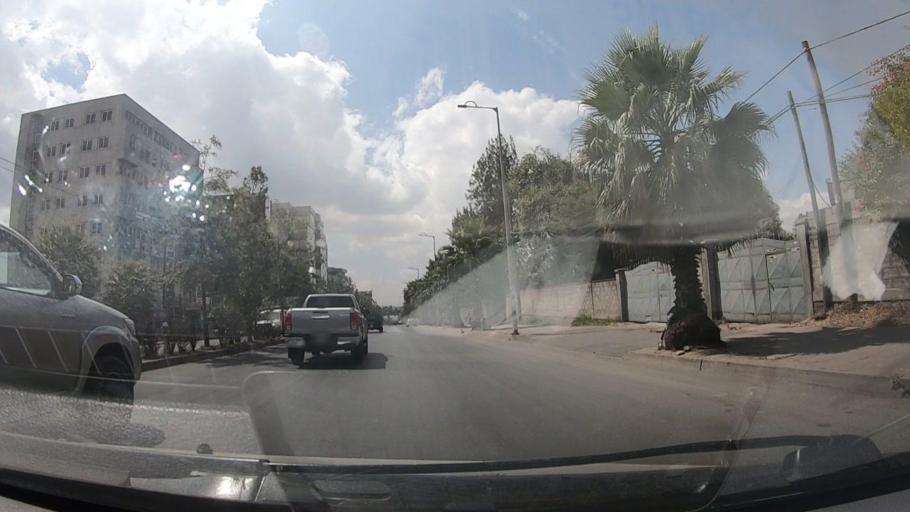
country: ET
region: Adis Abeba
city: Addis Ababa
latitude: 8.9911
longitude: 38.7252
